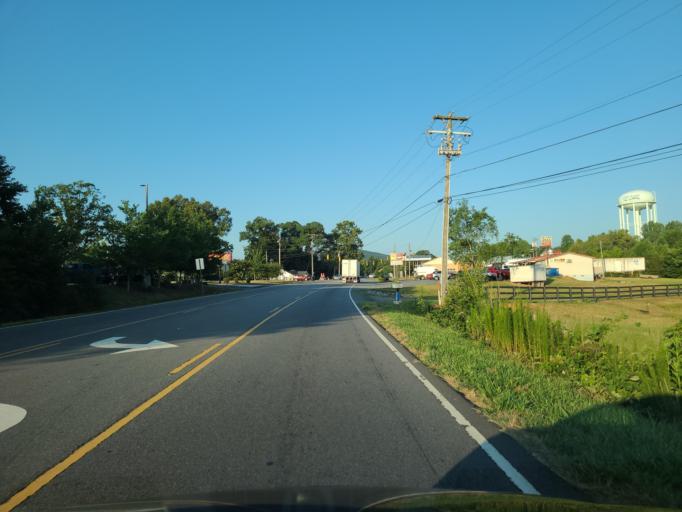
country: US
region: North Carolina
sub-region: Catawba County
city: Mountain View
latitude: 35.6815
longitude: -81.3766
